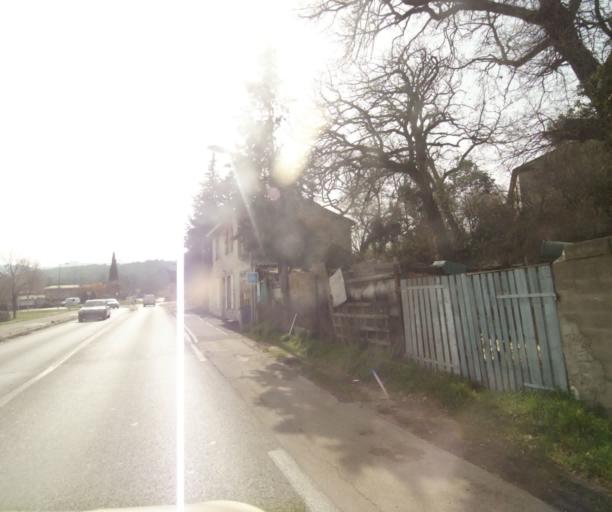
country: FR
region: Provence-Alpes-Cote d'Azur
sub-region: Departement des Bouches-du-Rhone
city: Gardanne
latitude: 43.4417
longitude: 5.4581
